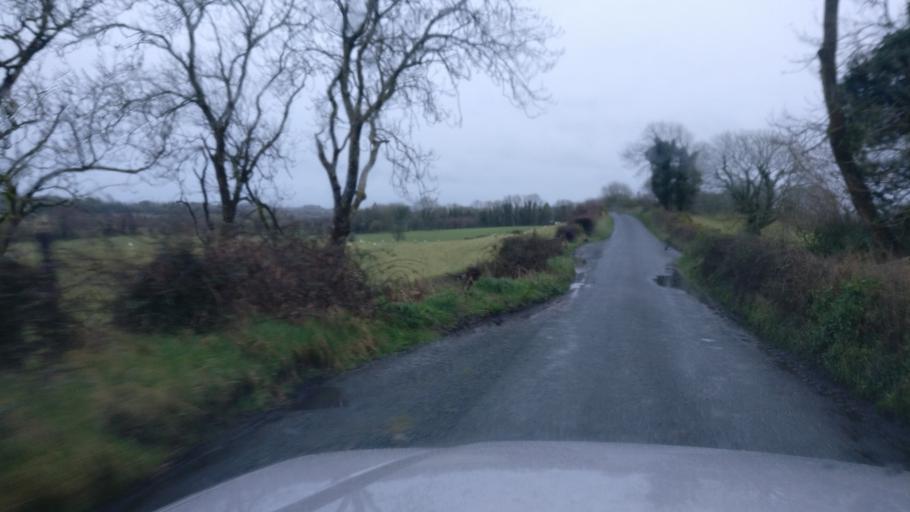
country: IE
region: Connaught
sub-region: County Galway
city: Ballinasloe
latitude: 53.3018
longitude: -8.2751
